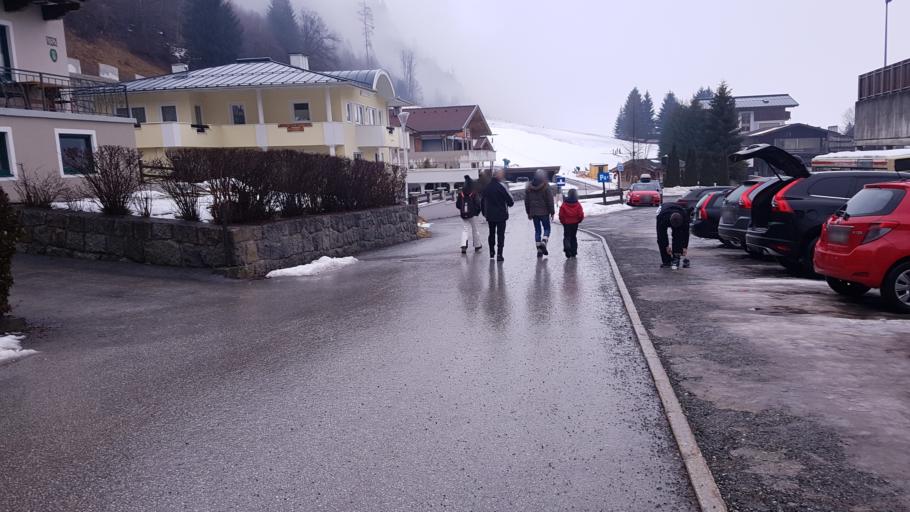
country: AT
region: Salzburg
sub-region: Politischer Bezirk Zell am See
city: Neukirchen am Grossvenediger
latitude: 47.2551
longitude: 12.2824
